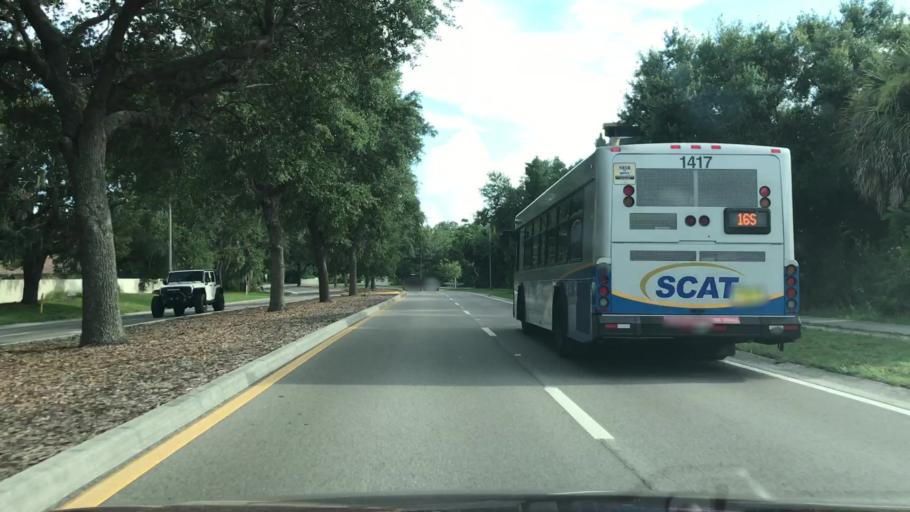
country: US
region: Florida
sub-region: Sarasota County
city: Venice Gardens
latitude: 27.0612
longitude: -82.3950
